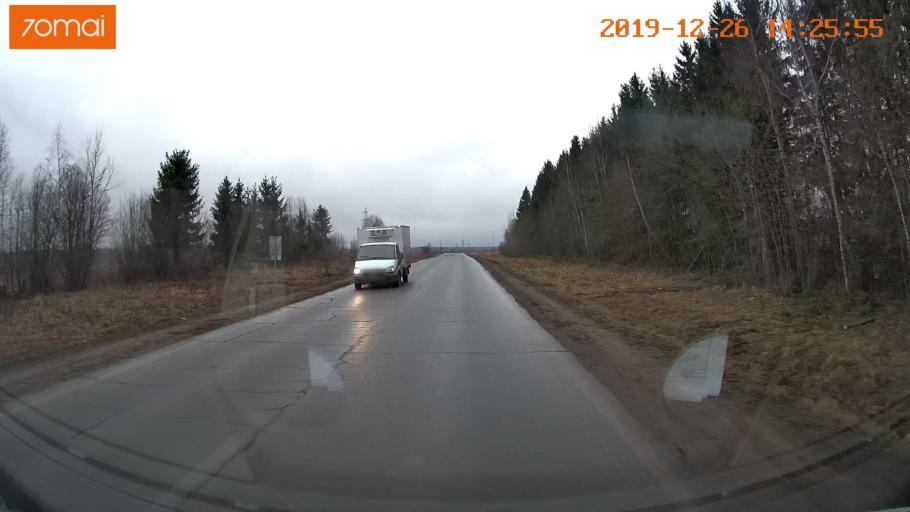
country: RU
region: Jaroslavl
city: Poshekhon'ye
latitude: 58.4903
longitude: 39.0909
